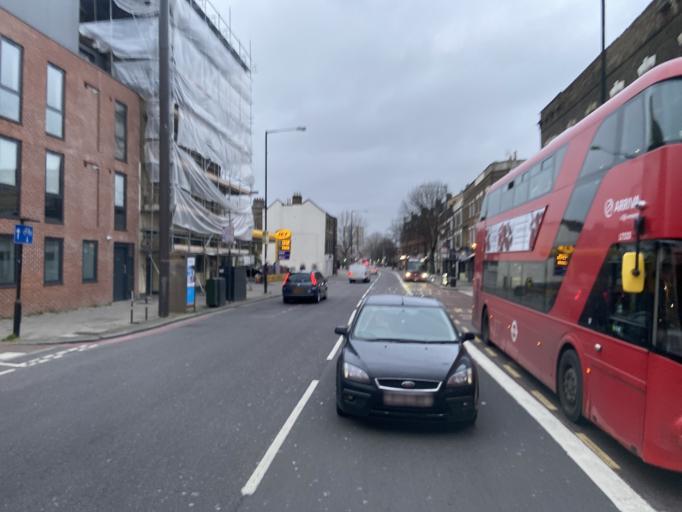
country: GB
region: England
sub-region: Greater London
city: Hackney
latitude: 51.5528
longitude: -0.0531
